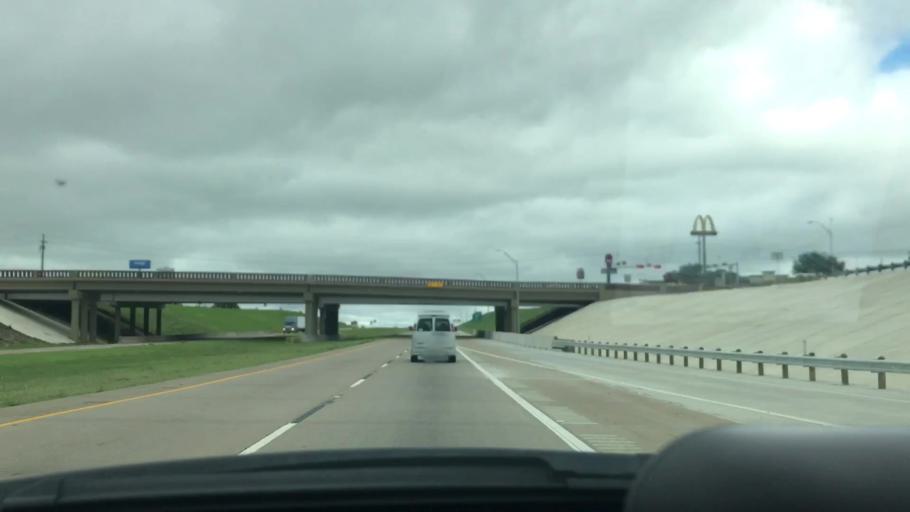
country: US
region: Texas
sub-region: Grayson County
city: Denison
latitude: 33.7610
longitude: -96.5851
